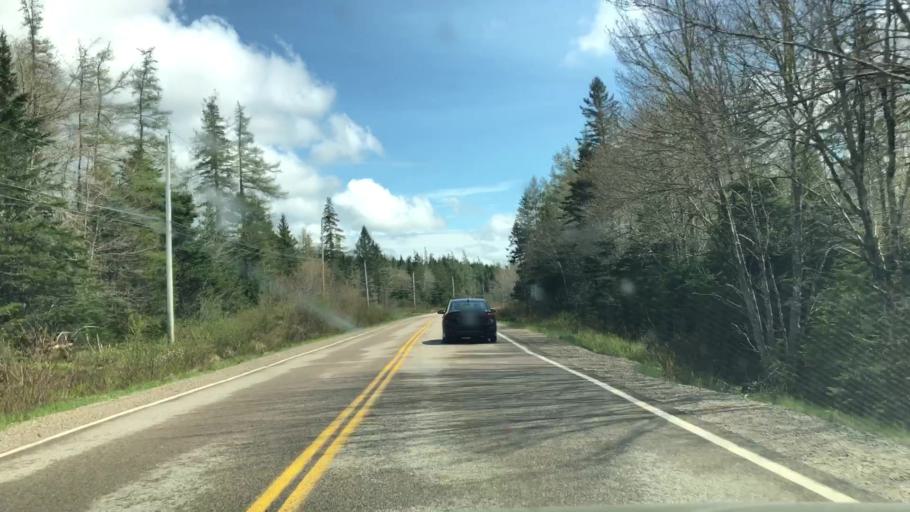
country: CA
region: Nova Scotia
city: Antigonish
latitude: 45.2113
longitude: -62.0046
